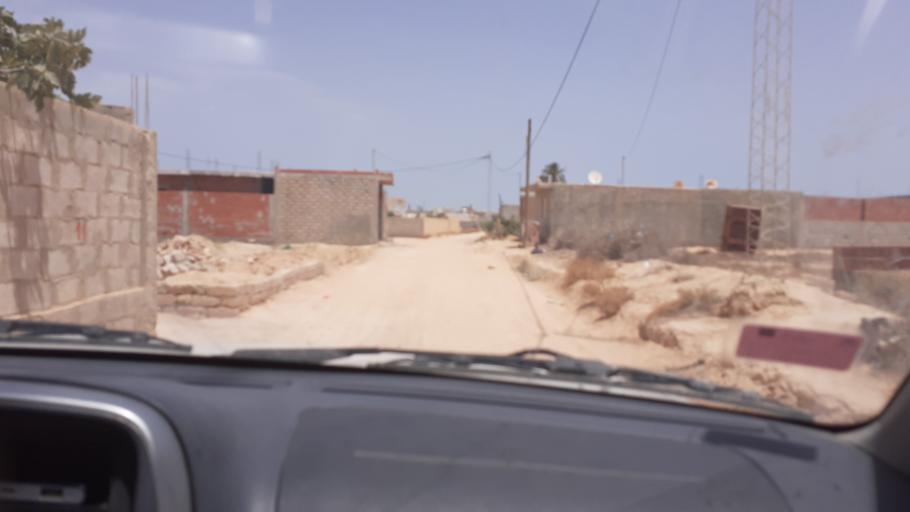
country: TN
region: Qabis
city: Matmata
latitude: 33.6093
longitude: 10.2895
